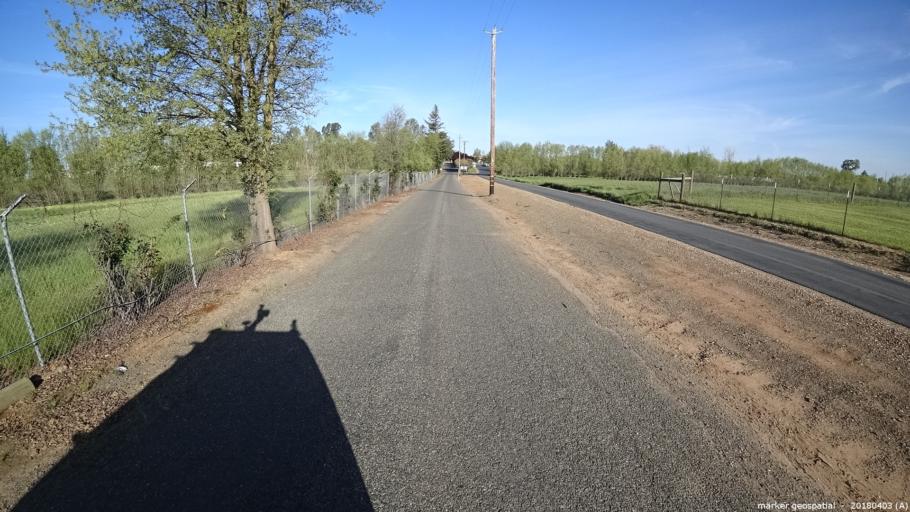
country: US
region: California
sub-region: Sacramento County
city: Wilton
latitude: 38.4462
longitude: -121.1967
